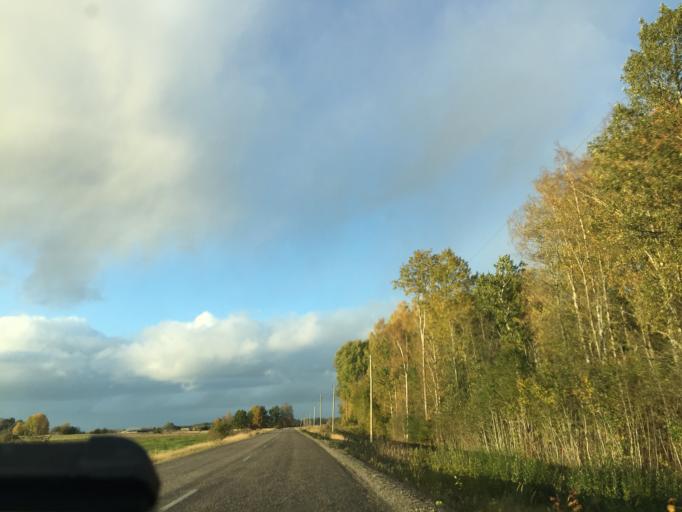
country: LV
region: Broceni
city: Broceni
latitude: 56.8707
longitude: 22.3817
